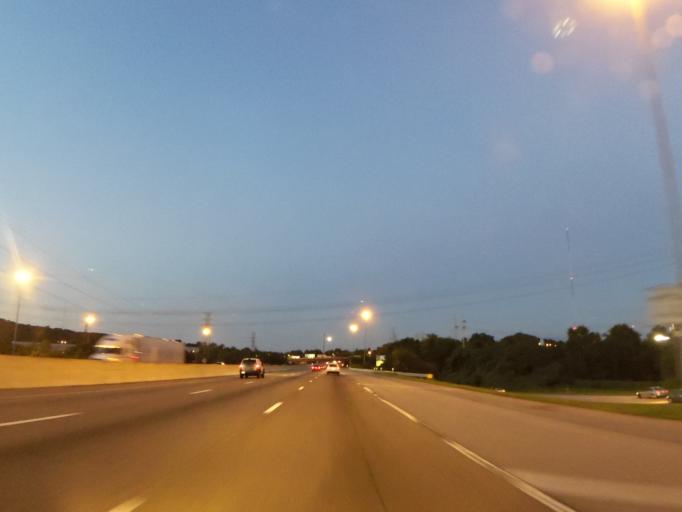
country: US
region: Tennessee
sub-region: Knox County
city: Knoxville
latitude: 35.9549
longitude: -83.9746
